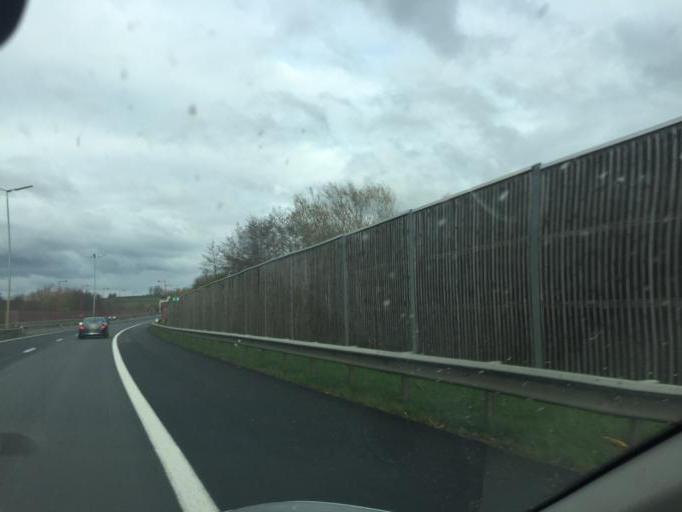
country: LU
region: Luxembourg
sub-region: Canton de Mersch
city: Mersch
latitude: 49.7467
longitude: 6.0902
